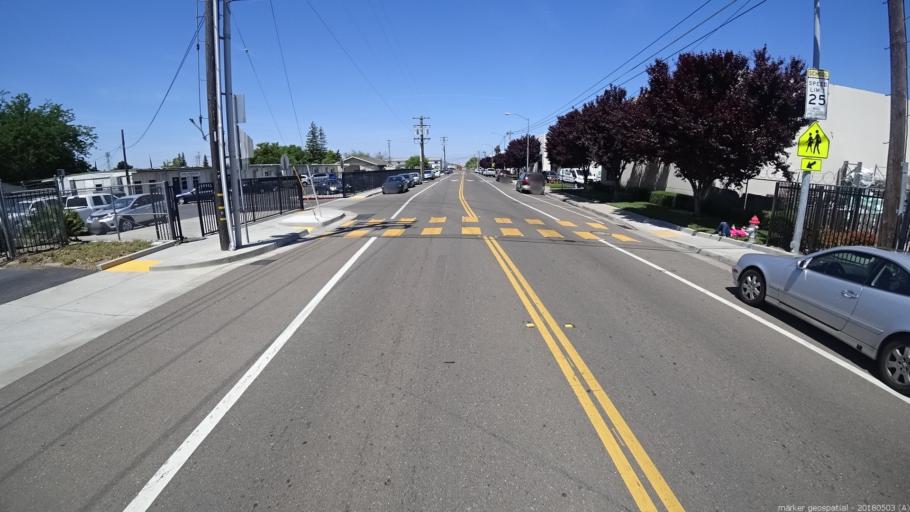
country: US
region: California
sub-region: Sacramento County
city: Rio Linda
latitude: 38.6454
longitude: -121.4200
